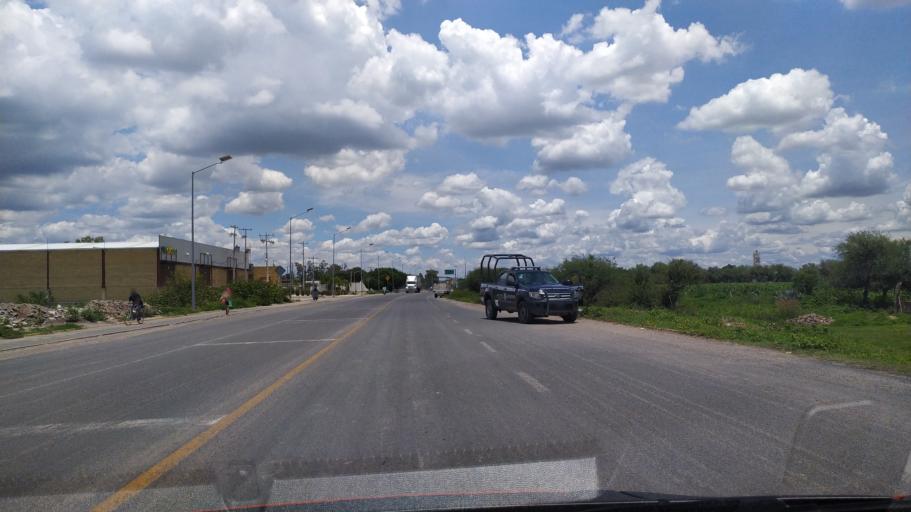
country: MX
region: Guanajuato
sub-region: San Francisco del Rincon
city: Fraccionamiento Villa Jardin
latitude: 20.9970
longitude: -101.8563
